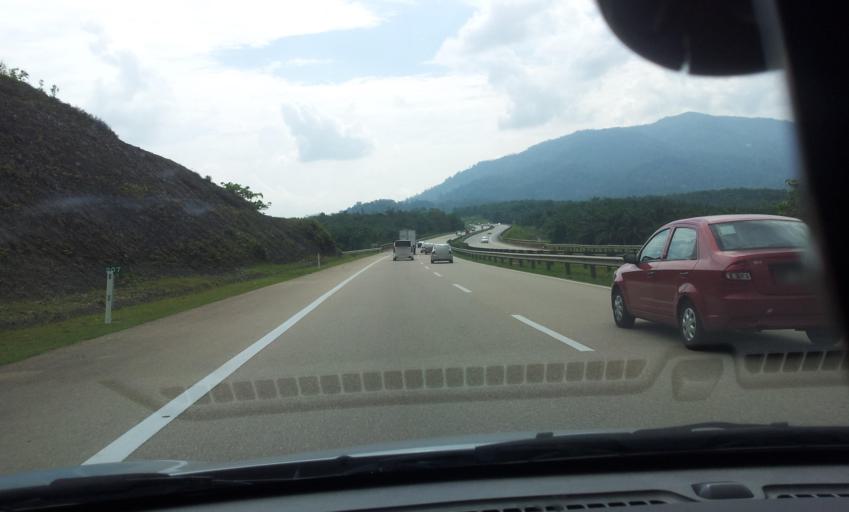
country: MY
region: Pahang
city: Kuantan
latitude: 3.7190
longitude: 103.0374
